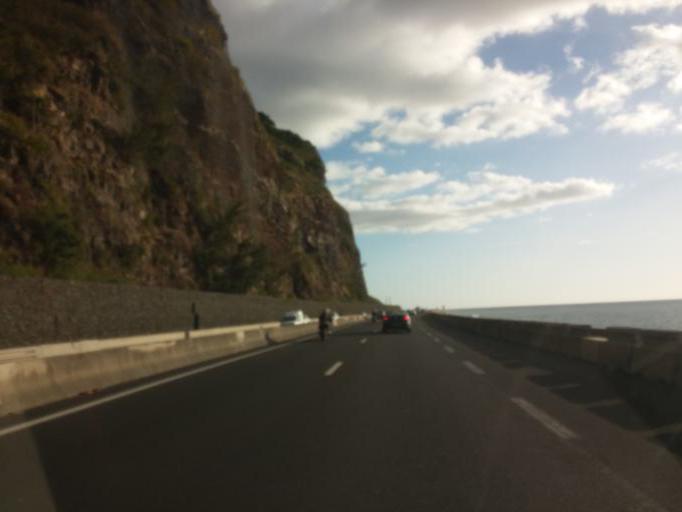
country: RE
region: Reunion
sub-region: Reunion
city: Saint-Denis
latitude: -20.8808
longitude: 55.3989
